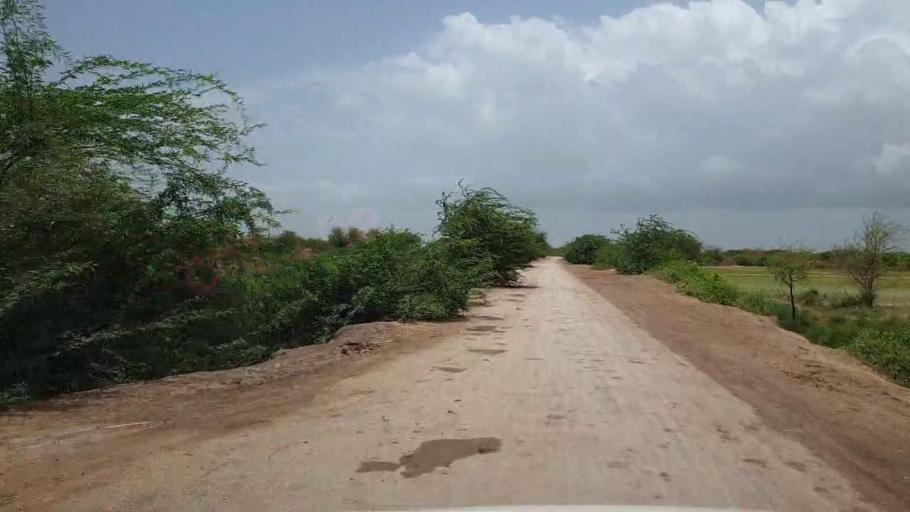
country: PK
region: Sindh
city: Kario
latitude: 24.6936
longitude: 68.6508
